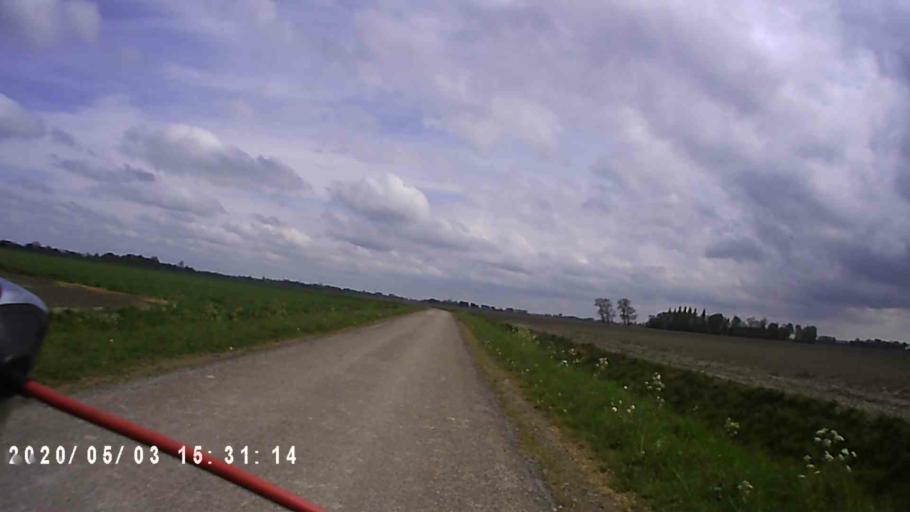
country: NL
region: Groningen
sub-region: Gemeente Winsum
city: Winsum
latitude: 53.3442
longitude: 6.4694
